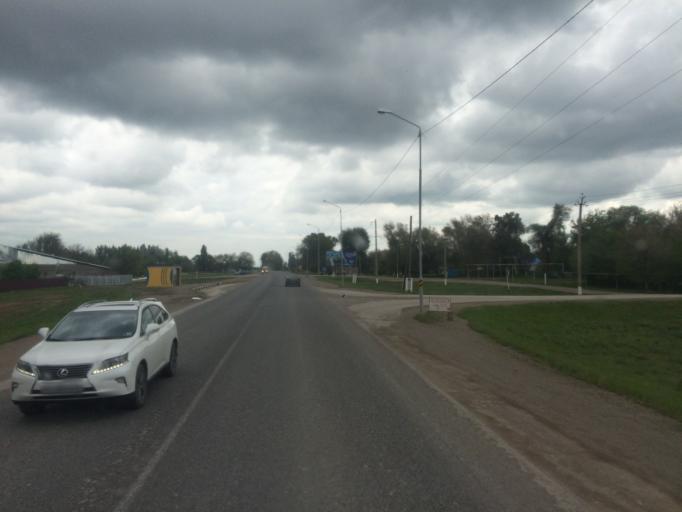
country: KZ
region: Zhambyl
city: Georgiyevka
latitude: 43.1431
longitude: 74.6161
